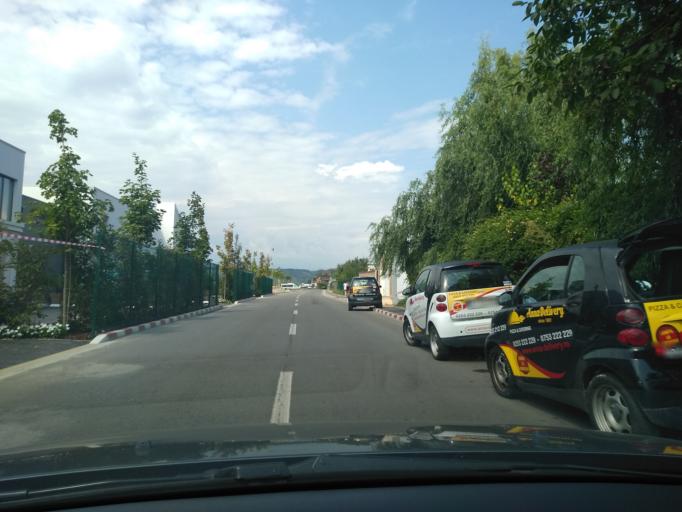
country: RO
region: Gorj
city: Targu Jiu
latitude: 45.0309
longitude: 23.2660
